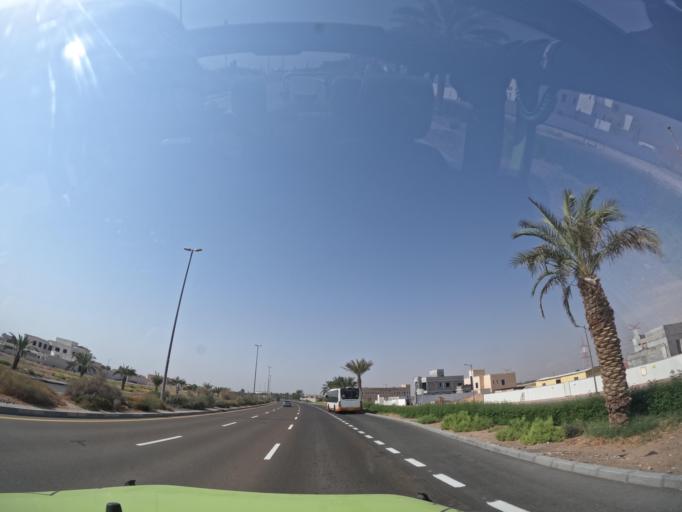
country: AE
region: Abu Dhabi
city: Al Ain
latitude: 24.2643
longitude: 55.6963
